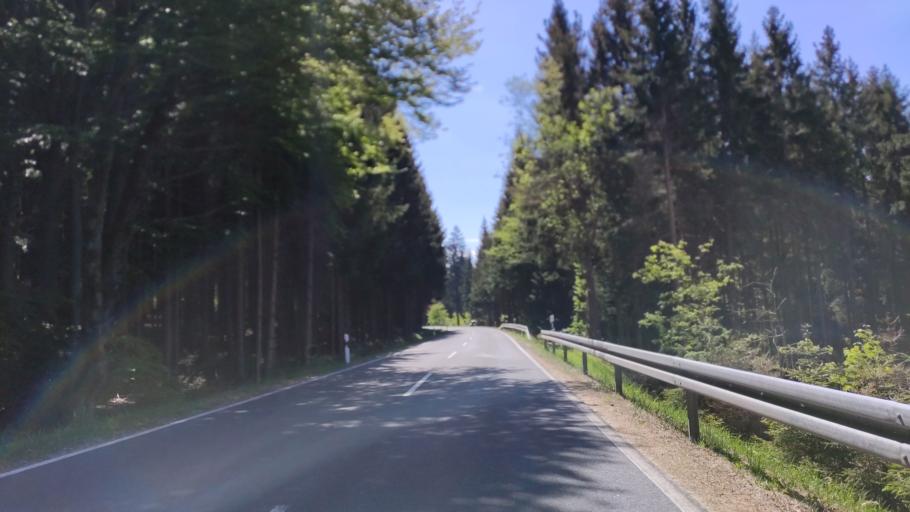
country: DE
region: Bavaria
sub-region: Upper Franconia
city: Reichenbach
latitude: 50.4430
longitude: 11.4139
